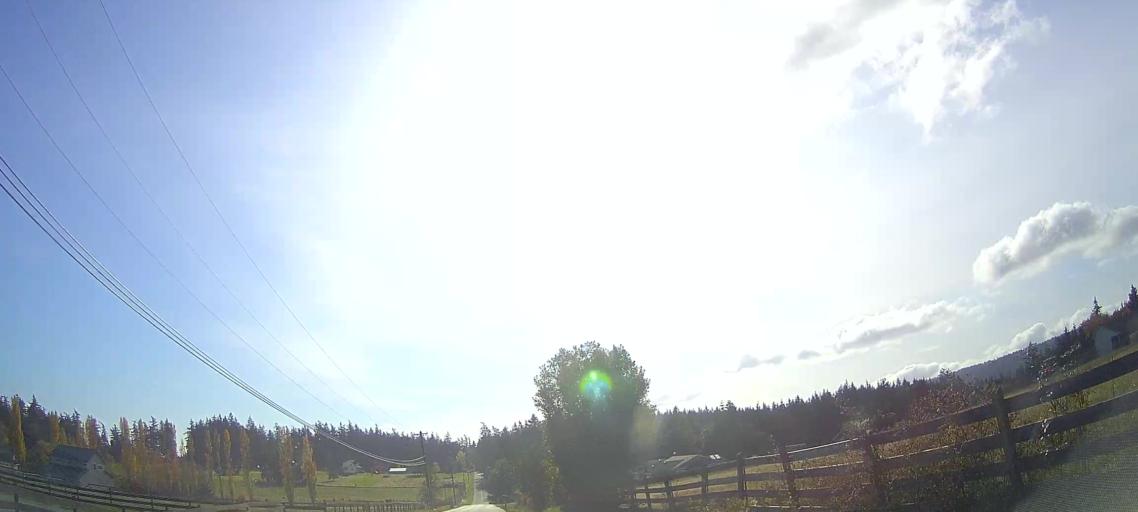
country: US
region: Washington
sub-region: Island County
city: Camano
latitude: 48.2052
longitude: -122.4563
